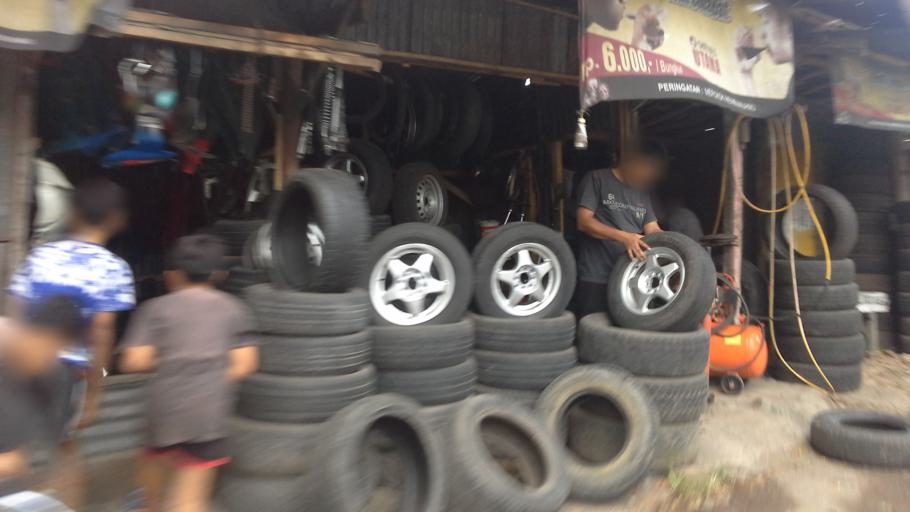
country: ID
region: East Java
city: Bondowoso
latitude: -7.9083
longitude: 113.8533
